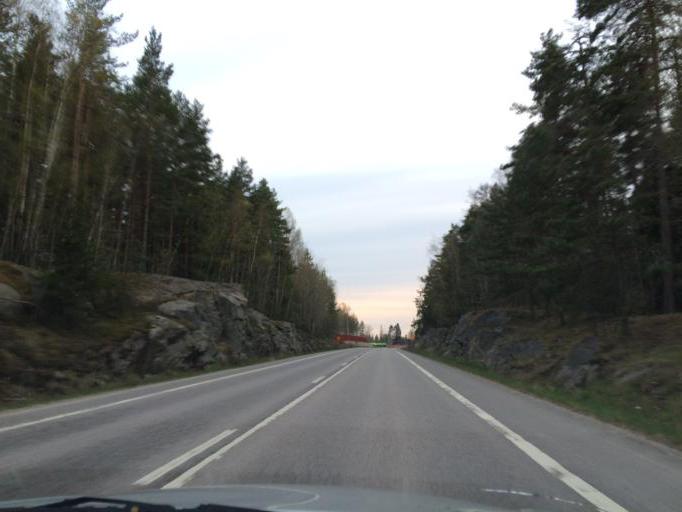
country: SE
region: Soedermanland
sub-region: Eskilstuna Kommun
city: Eskilstuna
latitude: 59.3988
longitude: 16.5557
